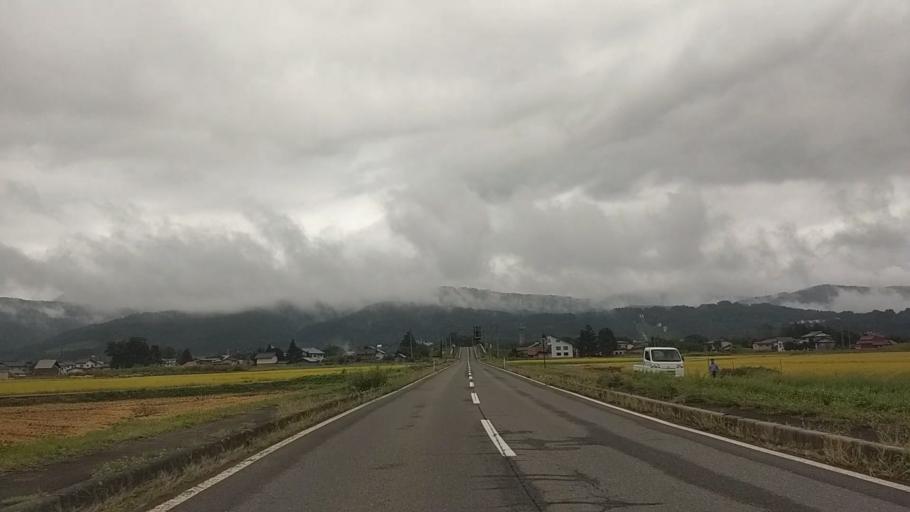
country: JP
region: Nagano
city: Iiyama
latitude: 36.8445
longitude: 138.3748
